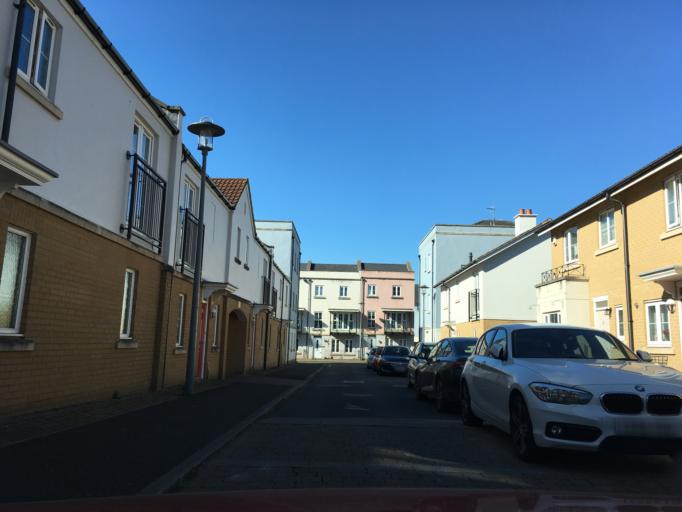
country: GB
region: England
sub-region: North Somerset
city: Portishead
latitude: 51.4917
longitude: -2.7599
